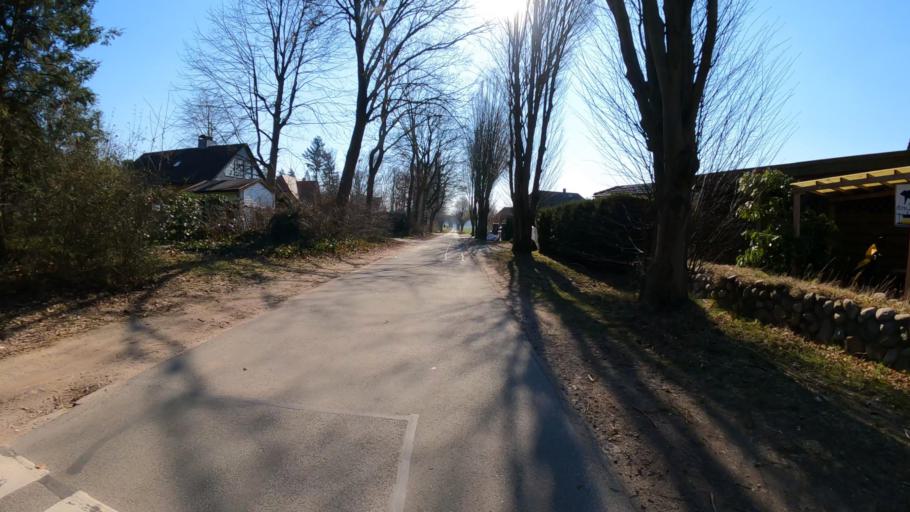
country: DE
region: Lower Saxony
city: Bendestorf
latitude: 53.3503
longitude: 9.9203
